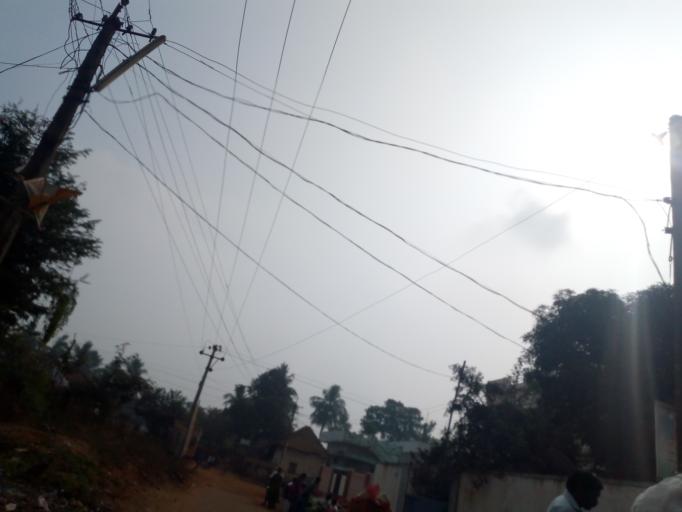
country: IN
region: Andhra Pradesh
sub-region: West Godavari
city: Tadepallegudem
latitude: 16.8372
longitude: 81.3480
